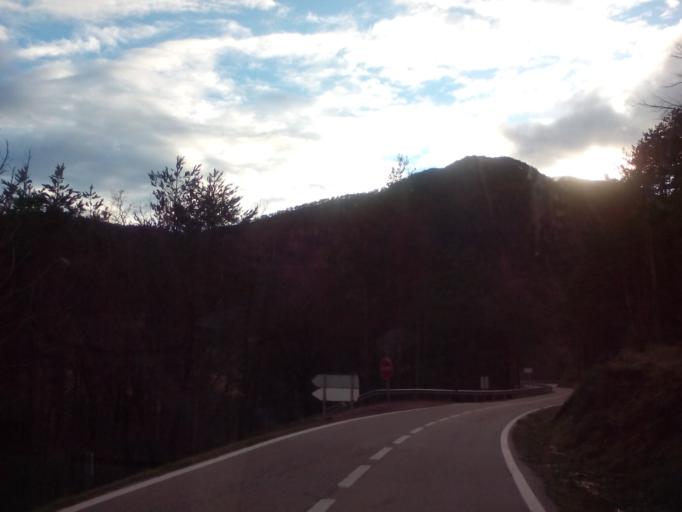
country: ES
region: Catalonia
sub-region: Provincia de Girona
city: Toses
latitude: 42.2742
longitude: 1.9918
